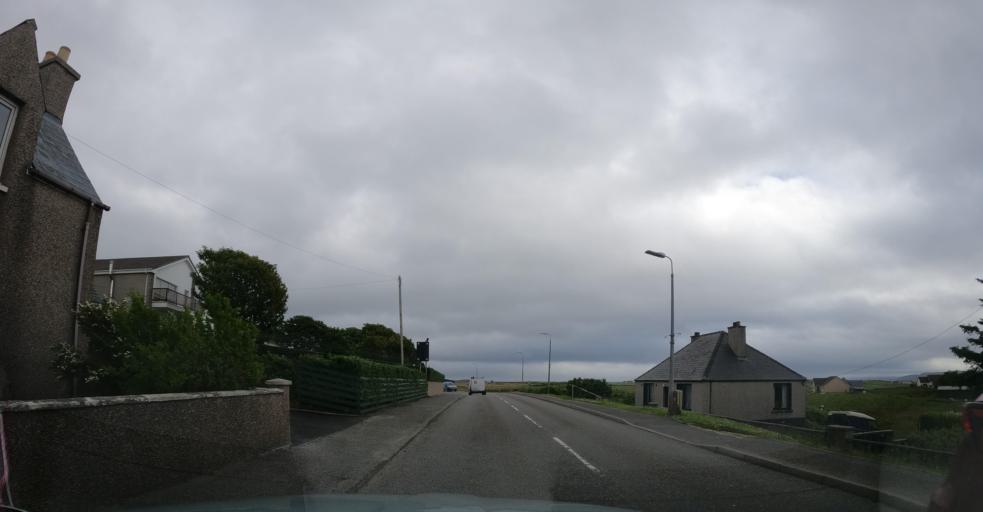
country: GB
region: Scotland
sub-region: Eilean Siar
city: Stornoway
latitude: 58.2040
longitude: -6.3513
